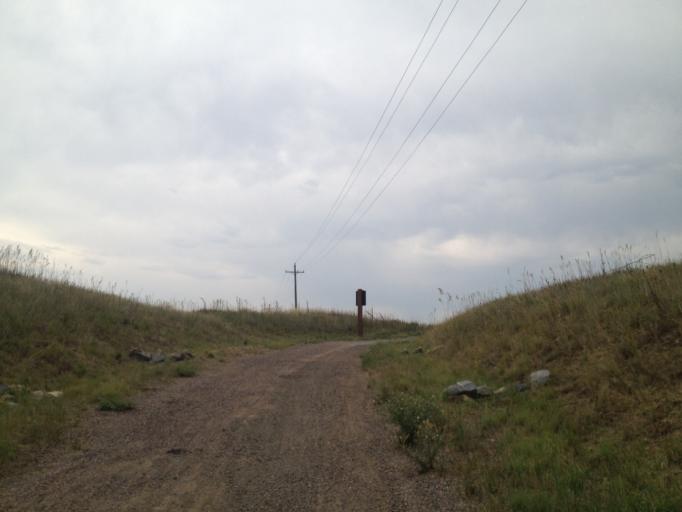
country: US
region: Colorado
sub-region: Boulder County
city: Lafayette
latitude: 40.0054
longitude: -105.0555
